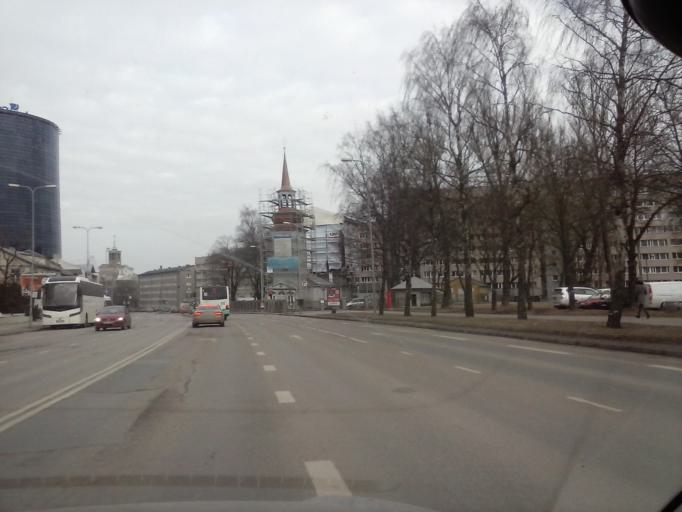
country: EE
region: Harju
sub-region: Tallinna linn
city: Tallinn
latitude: 59.4299
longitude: 24.7581
